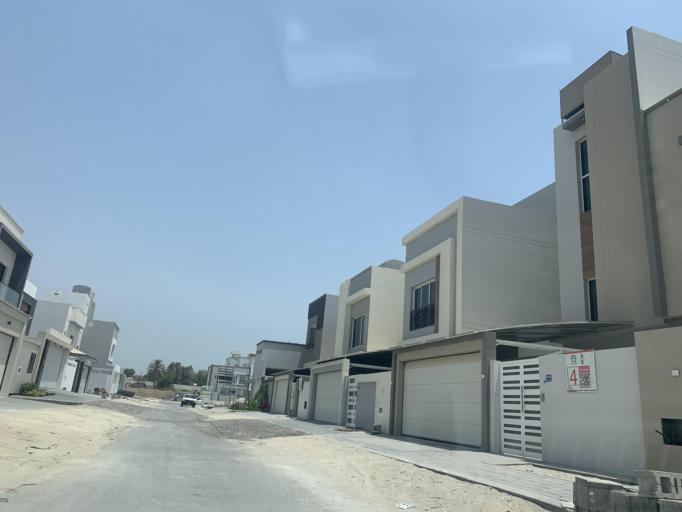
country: BH
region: Manama
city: Jidd Hafs
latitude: 26.2124
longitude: 50.4682
